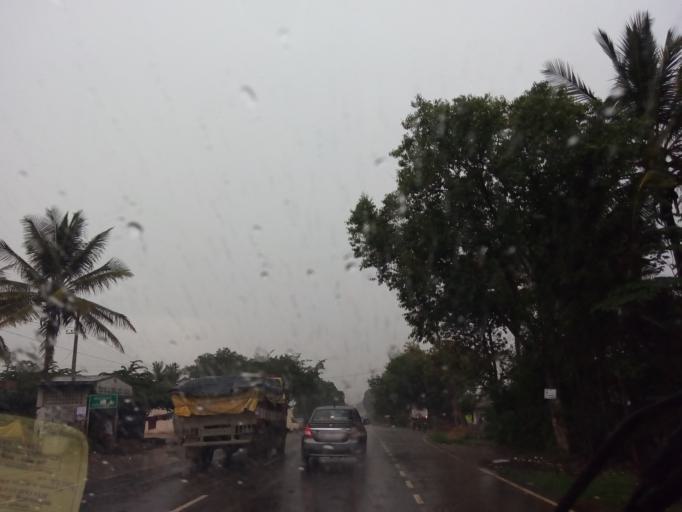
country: IN
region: Karnataka
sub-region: Hassan
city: Alur
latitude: 13.1182
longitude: 76.0027
